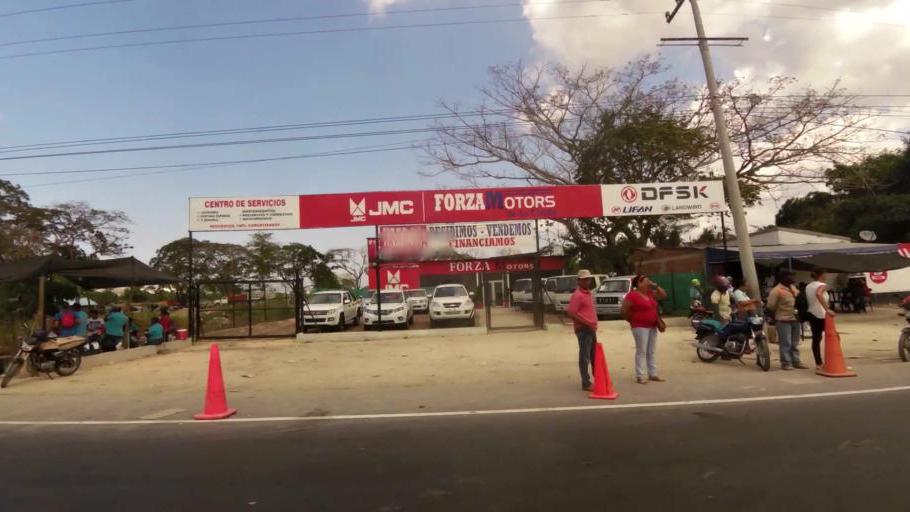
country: CO
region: Bolivar
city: Cartagena
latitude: 10.3760
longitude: -75.4599
